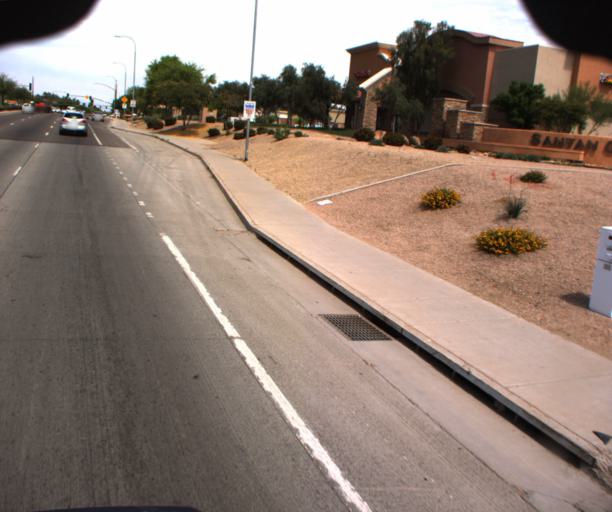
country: US
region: Arizona
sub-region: Maricopa County
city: Chandler
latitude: 33.2880
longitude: -111.8414
